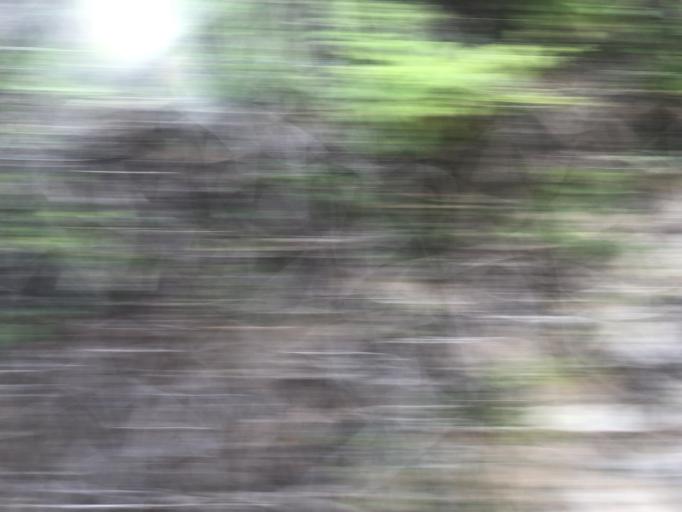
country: FR
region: Provence-Alpes-Cote d'Azur
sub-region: Departement des Alpes-Maritimes
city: Beaulieu-sur-Mer
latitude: 43.7124
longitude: 7.3323
